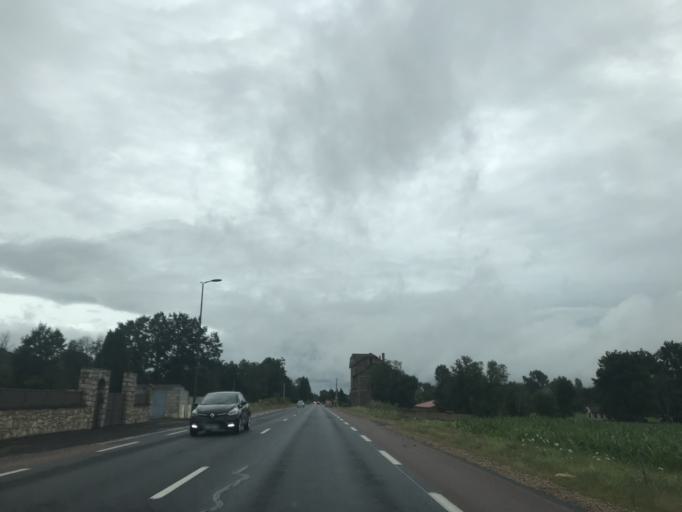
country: FR
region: Auvergne
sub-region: Departement du Puy-de-Dome
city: Arlanc
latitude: 45.4298
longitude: 3.7244
